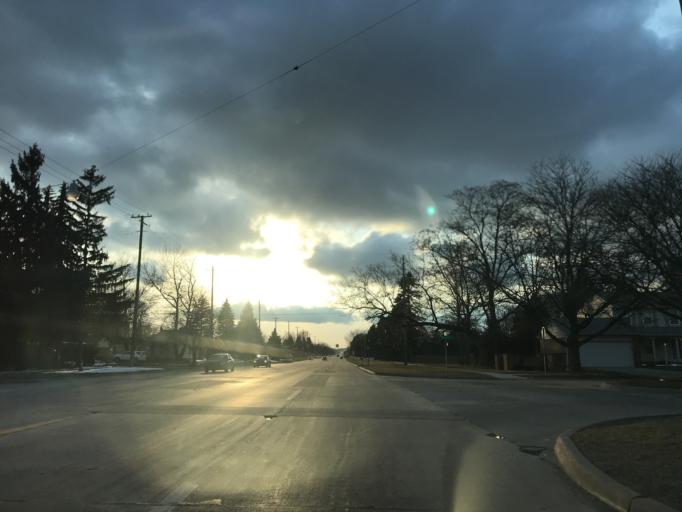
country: US
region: Michigan
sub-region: Oakland County
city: Farmington
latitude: 42.4260
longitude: -83.3819
